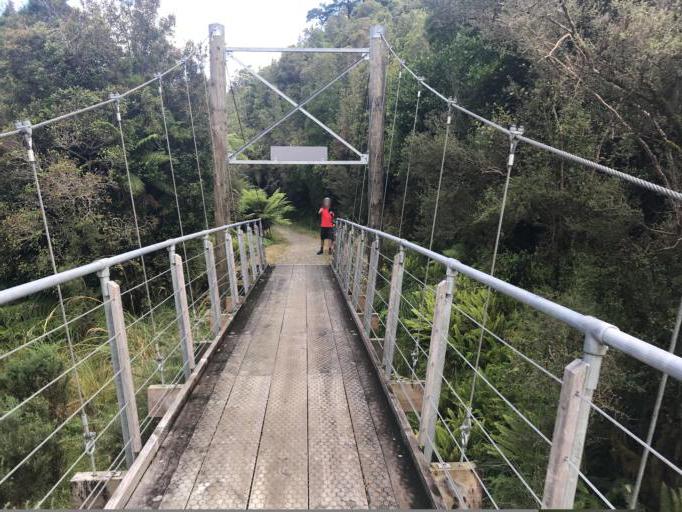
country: NZ
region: West Coast
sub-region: Westland District
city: Hokitika
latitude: -42.7654
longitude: 171.2487
